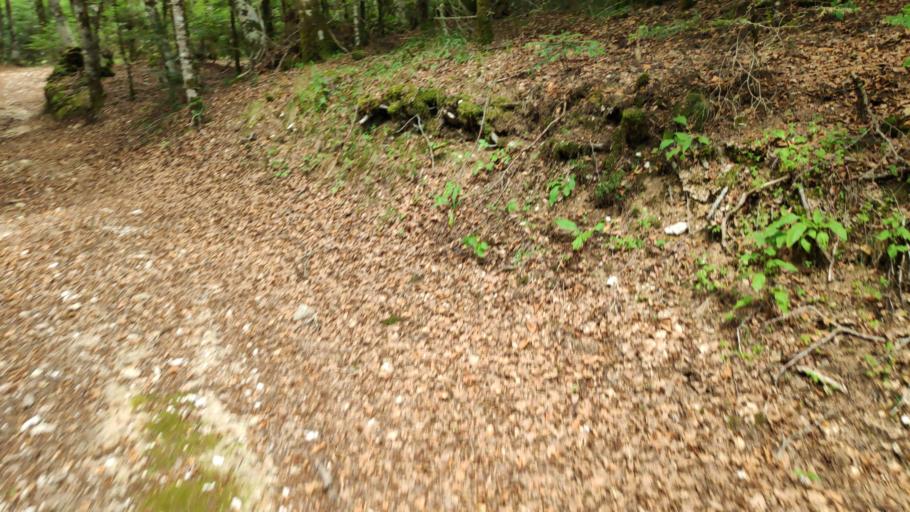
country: IT
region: Calabria
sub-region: Provincia di Vibo-Valentia
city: Serra San Bruno
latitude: 38.5425
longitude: 16.3649
